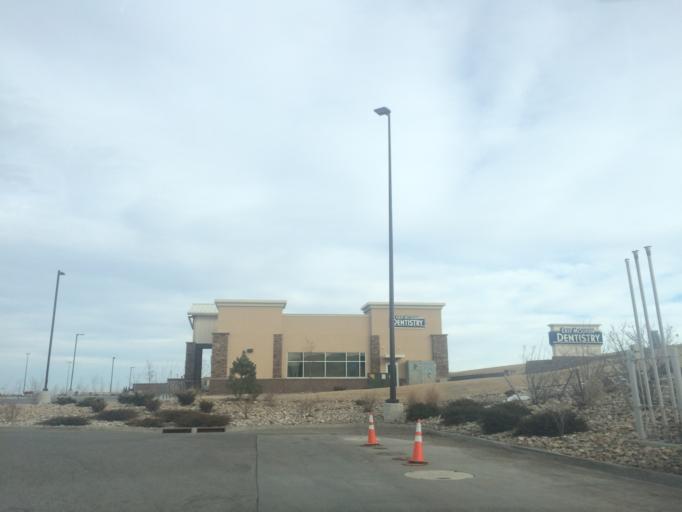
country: US
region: Colorado
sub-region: Boulder County
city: Erie
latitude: 40.0007
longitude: -105.0112
